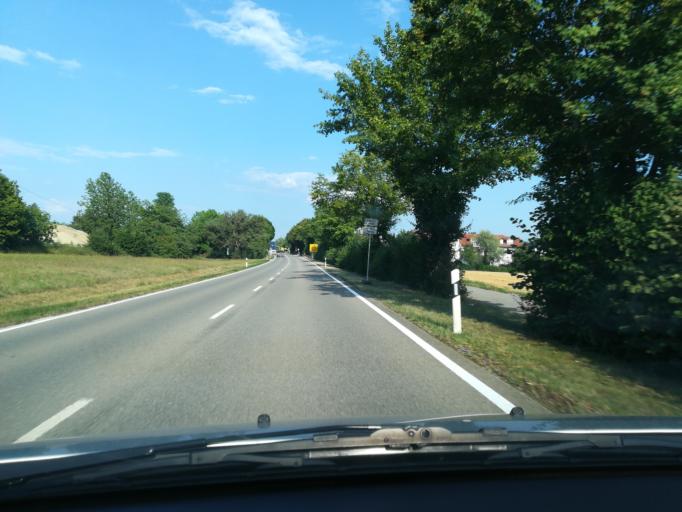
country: DE
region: Baden-Wuerttemberg
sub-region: Freiburg Region
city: Gottmadingen
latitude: 47.7369
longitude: 8.7647
